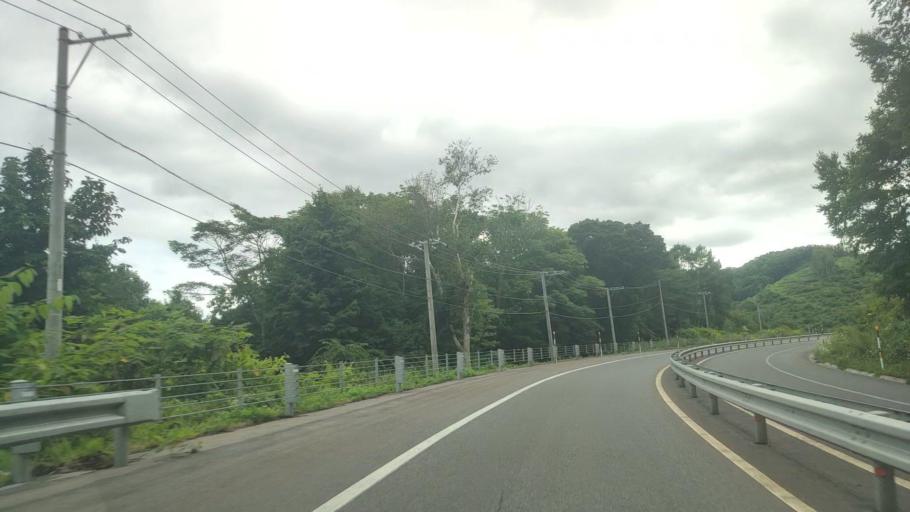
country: JP
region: Hokkaido
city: Niseko Town
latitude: 42.5983
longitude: 140.5803
